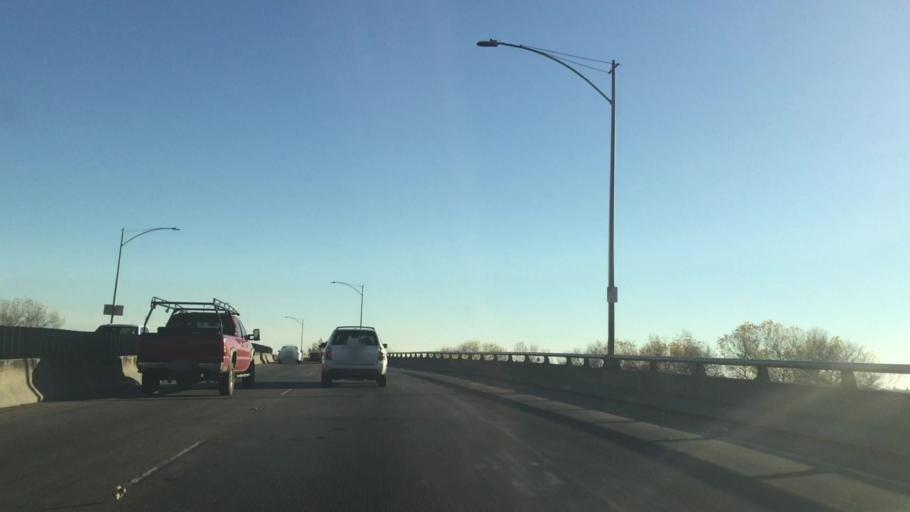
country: US
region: California
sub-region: Yuba County
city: Marysville
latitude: 39.1343
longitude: -121.5896
